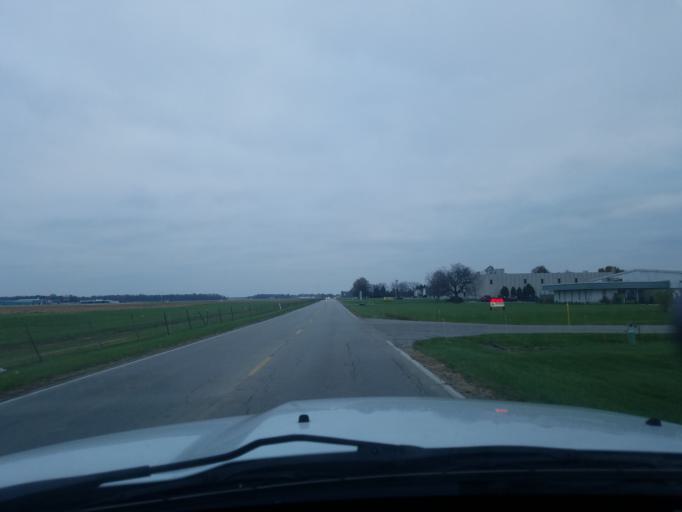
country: US
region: Indiana
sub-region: Delaware County
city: Muncie
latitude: 40.2335
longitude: -85.3978
